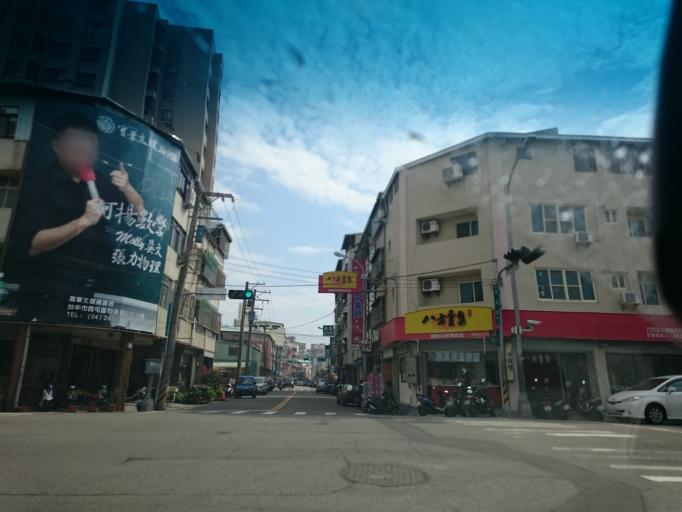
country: TW
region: Taiwan
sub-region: Taichung City
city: Taichung
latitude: 24.1824
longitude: 120.6425
